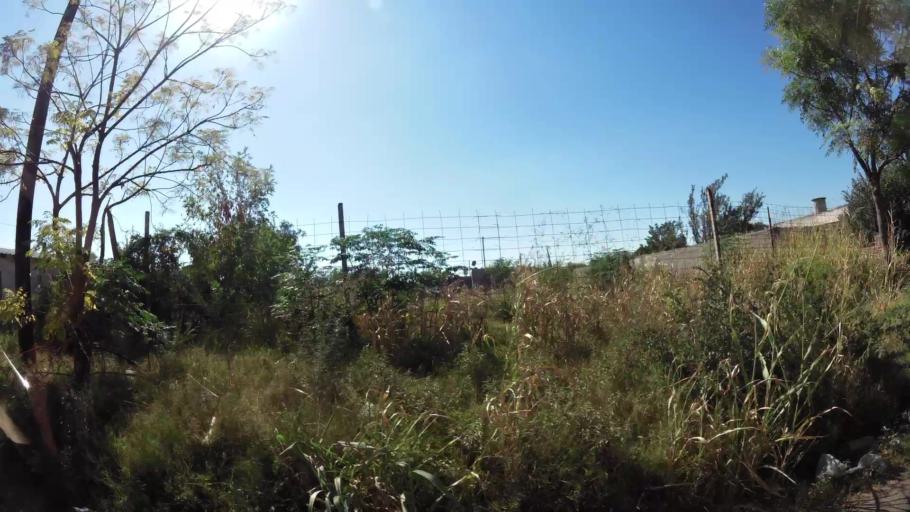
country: AR
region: Cordoba
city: Villa Allende
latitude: -31.3245
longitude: -64.2447
